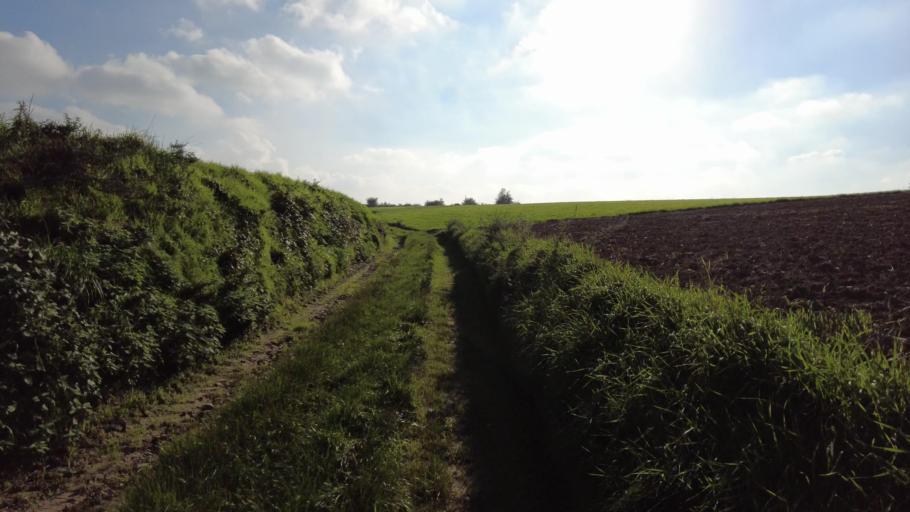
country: BE
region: Wallonia
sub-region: Province du Brabant Wallon
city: Jodoigne
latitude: 50.7302
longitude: 4.8982
